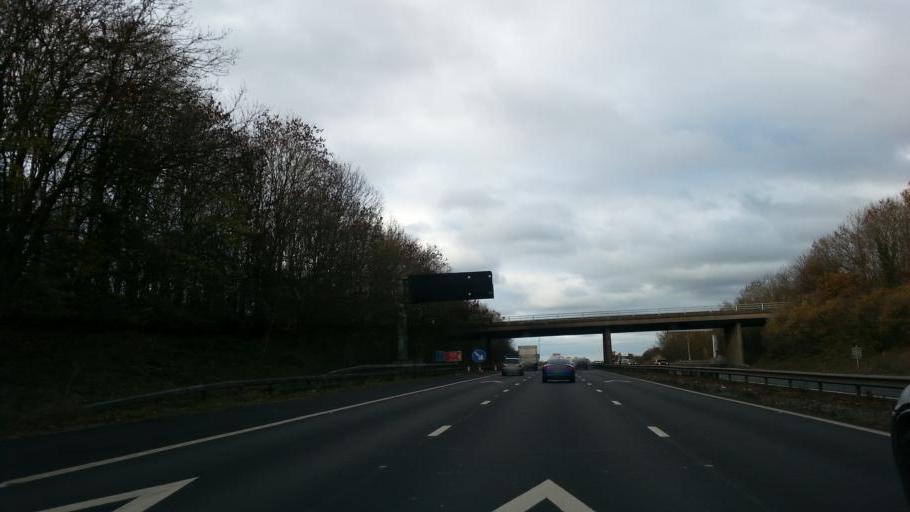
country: GB
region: England
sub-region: Warwickshire
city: Long Lawford
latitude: 52.4146
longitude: -1.2825
